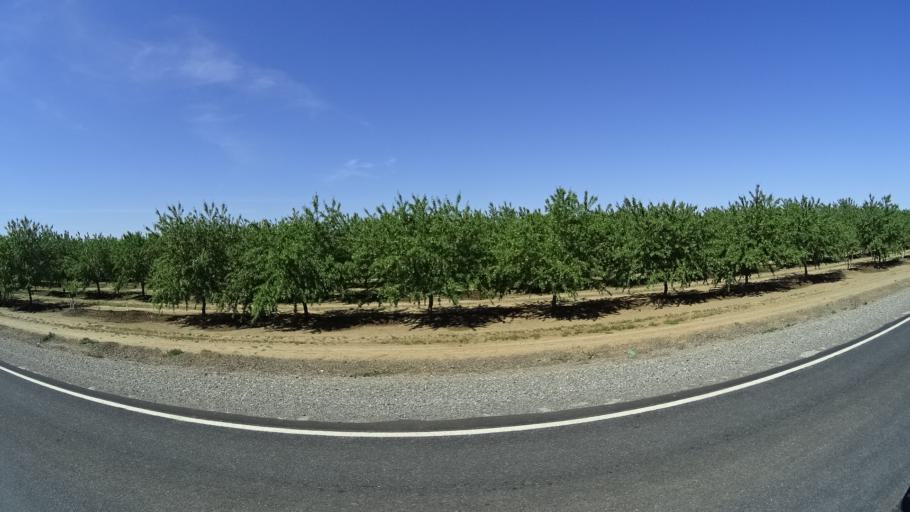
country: US
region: California
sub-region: Glenn County
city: Willows
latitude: 39.6359
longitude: -122.1411
